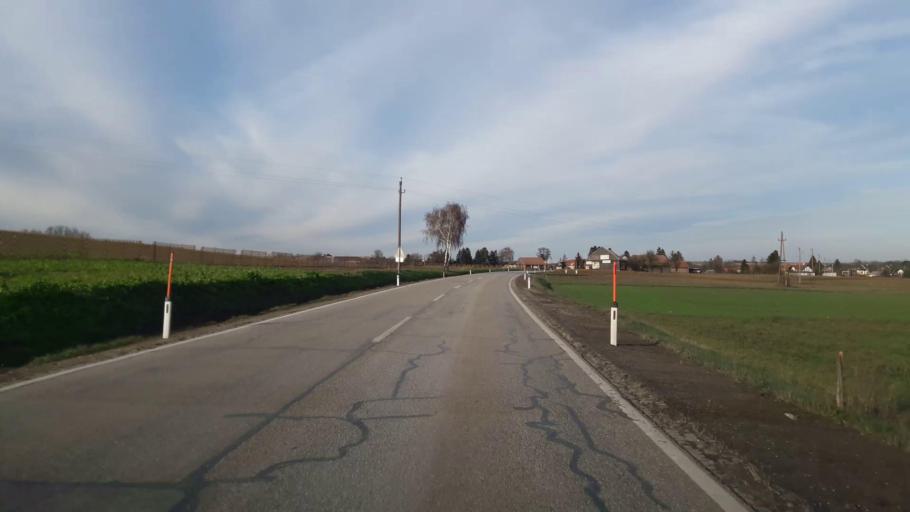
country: AT
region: Lower Austria
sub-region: Politischer Bezirk Ganserndorf
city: Bad Pirawarth
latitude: 48.4414
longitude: 16.6053
